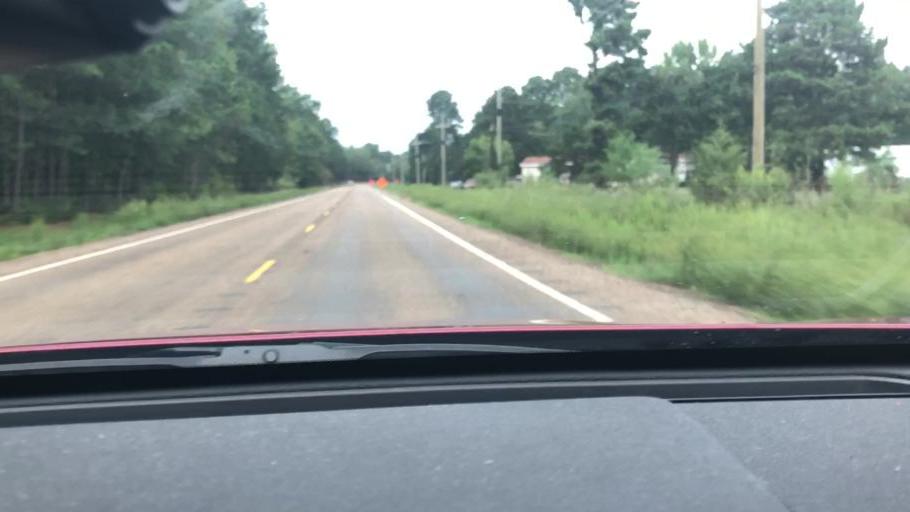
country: US
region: Texas
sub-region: Bowie County
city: Wake Village
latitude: 33.3806
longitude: -94.1040
